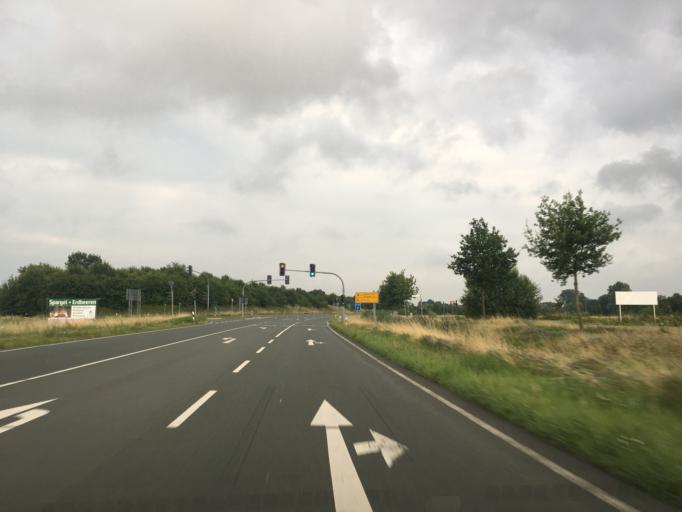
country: DE
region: North Rhine-Westphalia
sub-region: Regierungsbezirk Munster
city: Greven
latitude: 52.0441
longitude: 7.6205
